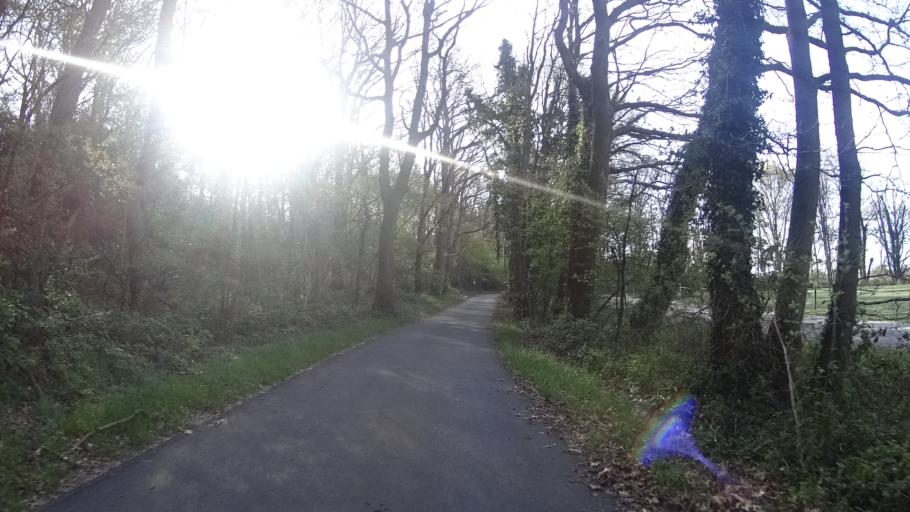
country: DE
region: Lower Saxony
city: Haren
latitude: 52.8084
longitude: 7.2551
